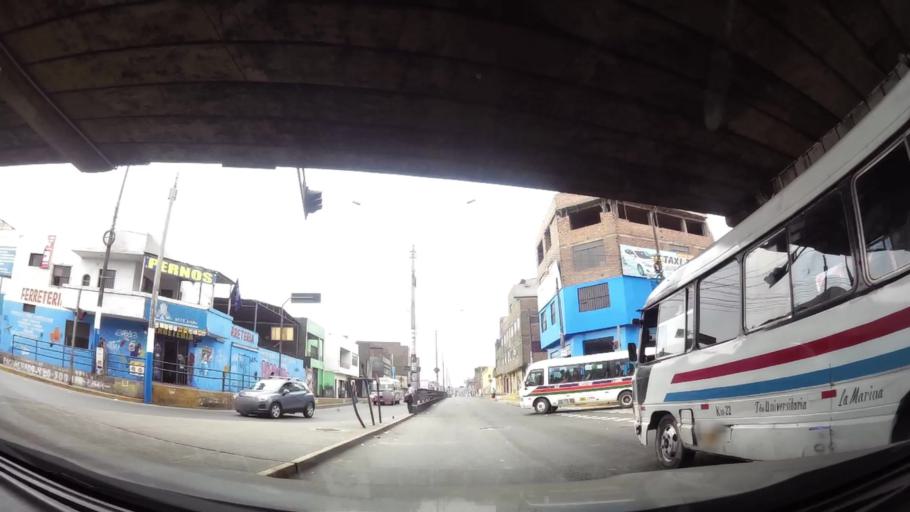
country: PE
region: Callao
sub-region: Callao
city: Callao
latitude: -12.0319
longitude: -77.0775
